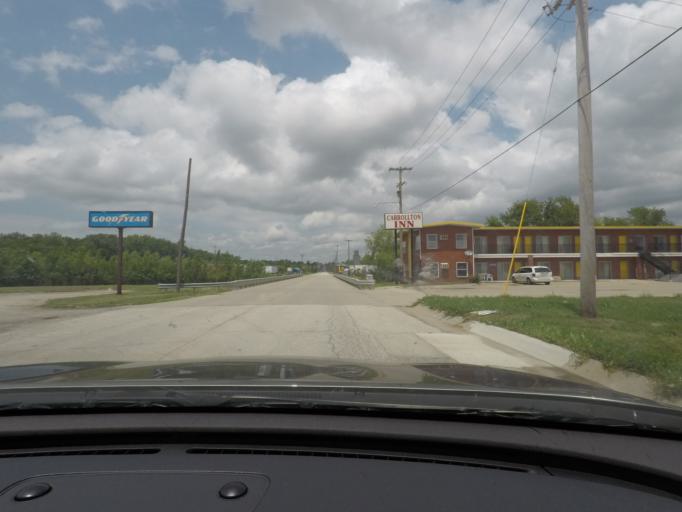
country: US
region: Missouri
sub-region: Carroll County
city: Carrollton
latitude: 39.3427
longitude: -93.4958
